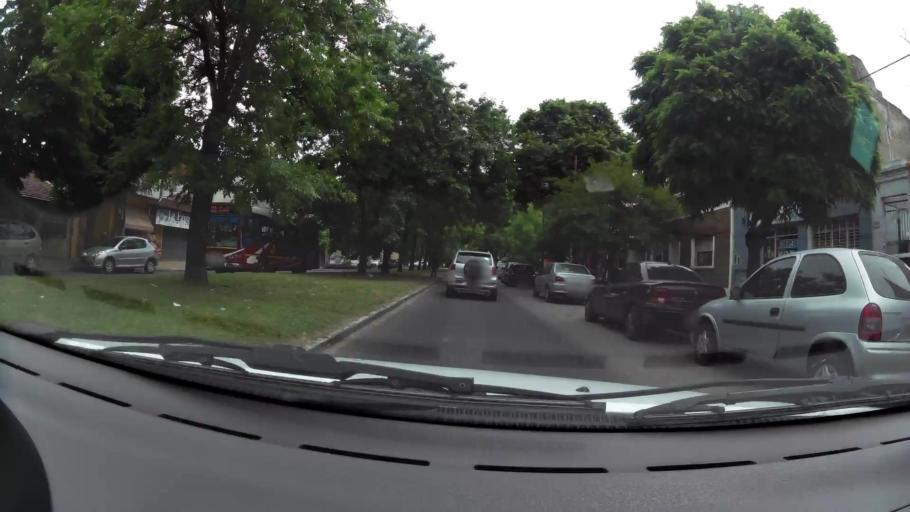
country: AR
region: Buenos Aires
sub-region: Partido de La Plata
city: La Plata
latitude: -34.9389
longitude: -57.9614
